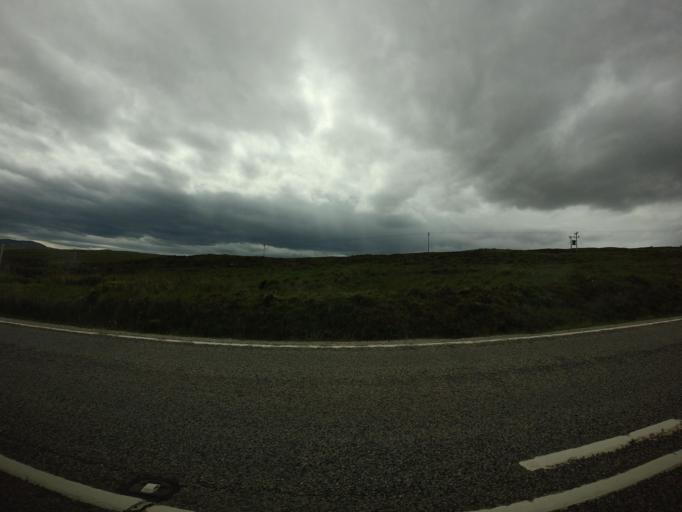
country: GB
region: Scotland
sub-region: Highland
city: Muir of Ord
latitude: 57.6931
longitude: -4.7776
